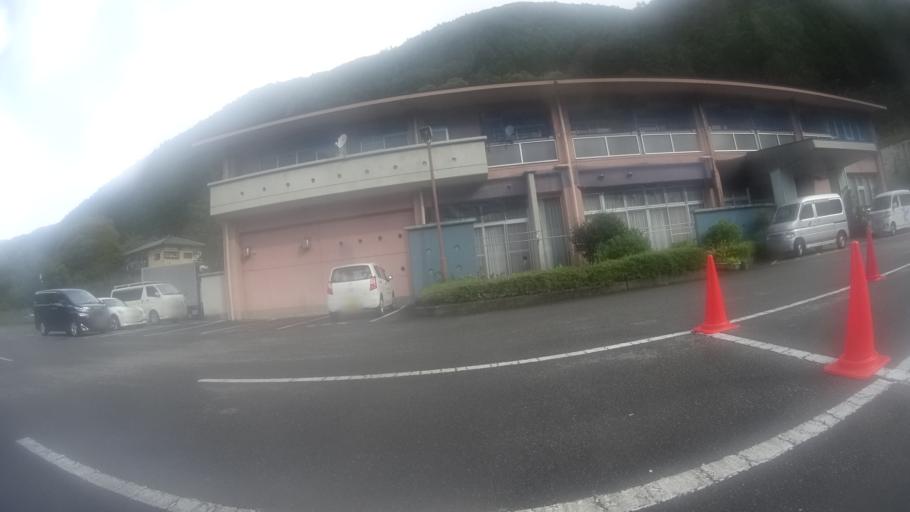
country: JP
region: Yamanashi
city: Otsuki
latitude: 35.7894
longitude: 138.9240
